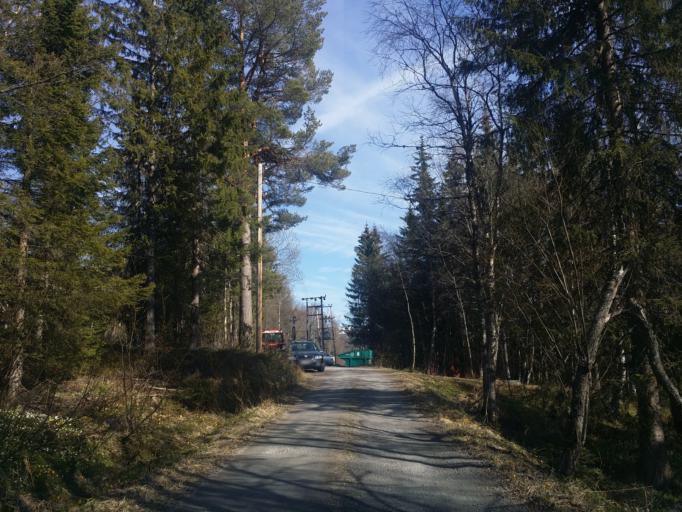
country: NO
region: Telemark
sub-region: Seljord
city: Seljord
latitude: 59.6229
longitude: 8.6852
